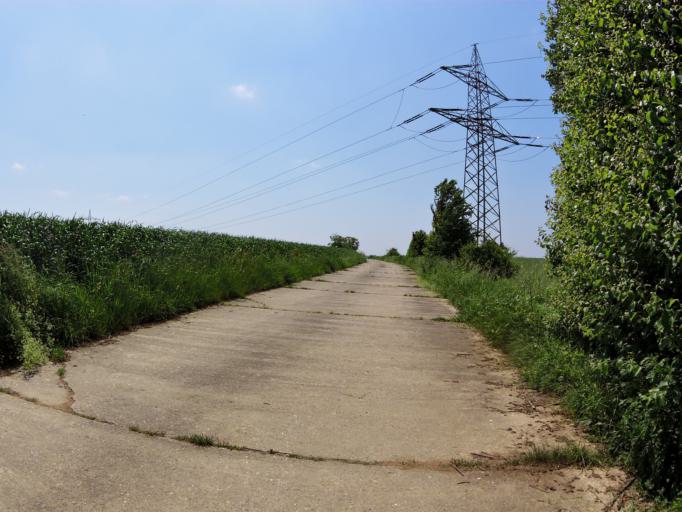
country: DE
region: Bavaria
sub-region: Regierungsbezirk Unterfranken
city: Kleinrinderfeld
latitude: 49.7097
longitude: 9.8479
